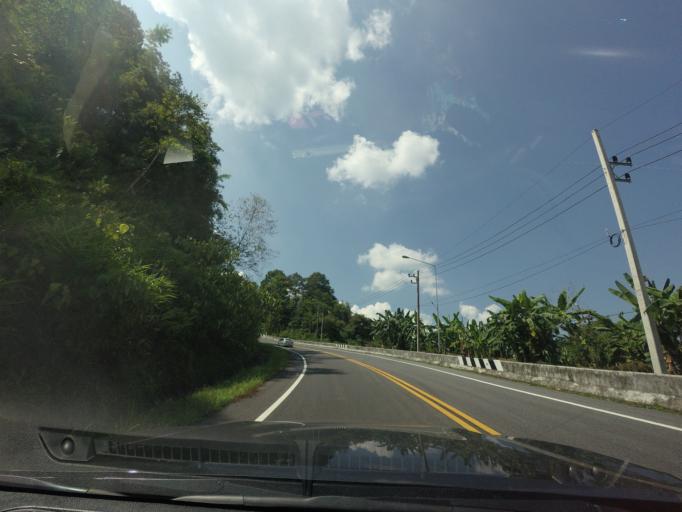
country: TH
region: Nan
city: Bo Kluea
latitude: 19.0826
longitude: 101.1477
